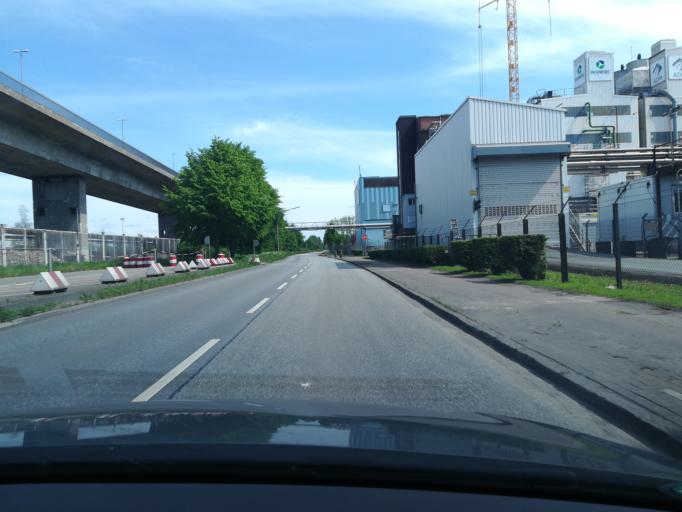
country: DE
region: Hamburg
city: Altona
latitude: 53.5185
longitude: 9.9535
